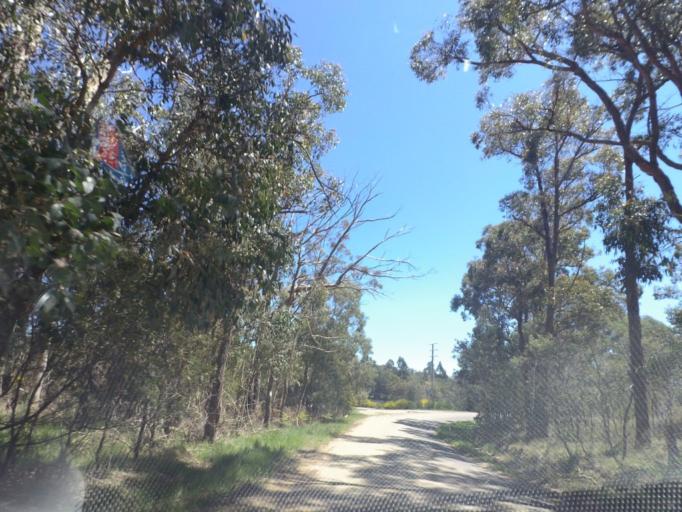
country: AU
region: Victoria
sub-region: Hume
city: Sunbury
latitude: -37.3825
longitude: 144.5516
